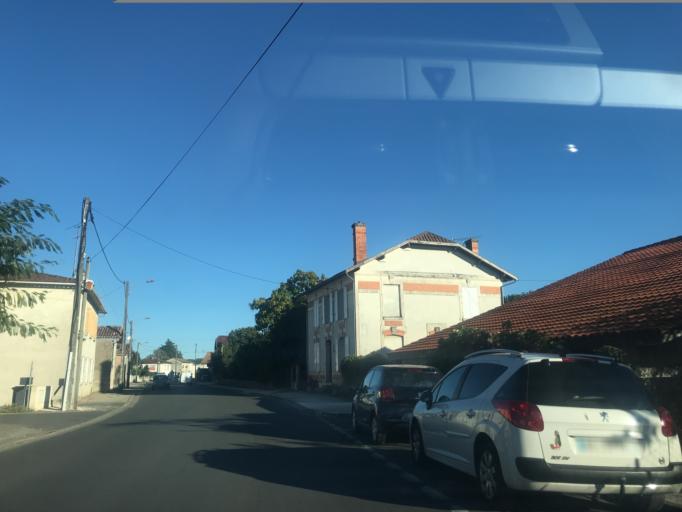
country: FR
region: Poitou-Charentes
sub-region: Departement de la Charente-Maritime
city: Saint-Aigulin
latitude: 45.1596
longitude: -0.0167
